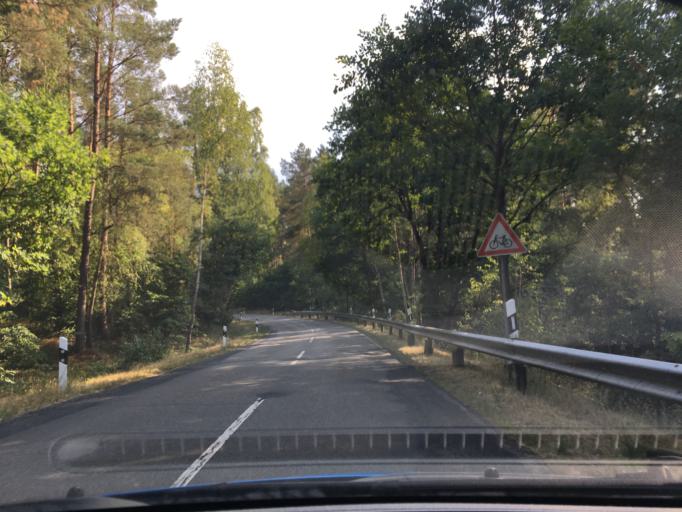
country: DE
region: Lower Saxony
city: Hitzacker
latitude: 53.1657
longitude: 11.0210
